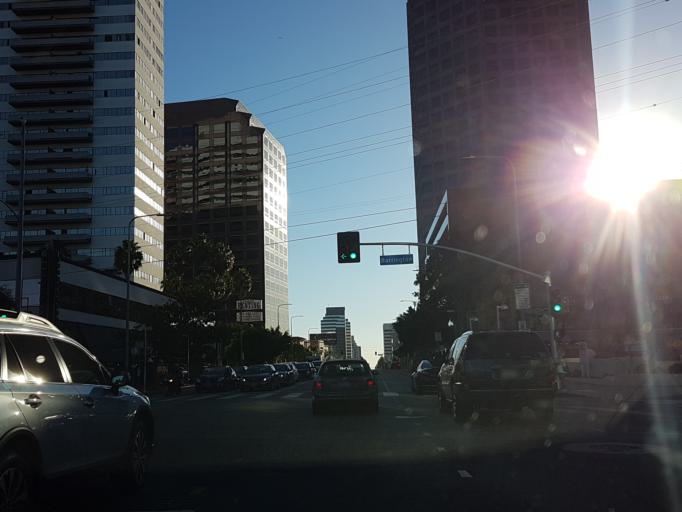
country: US
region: California
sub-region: Los Angeles County
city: Westwood, Los Angeles
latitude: 34.0496
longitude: -118.4608
